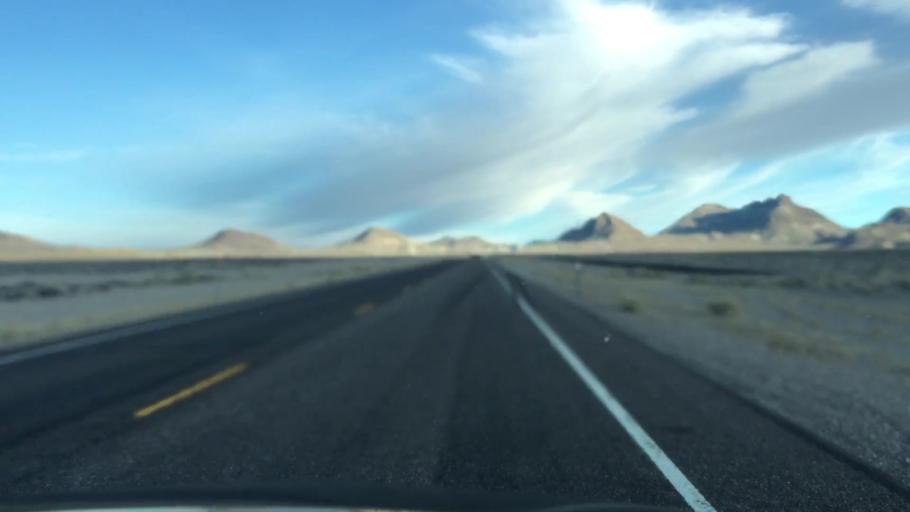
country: US
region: Nevada
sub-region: Nye County
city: Tonopah
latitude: 38.0872
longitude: -117.2880
